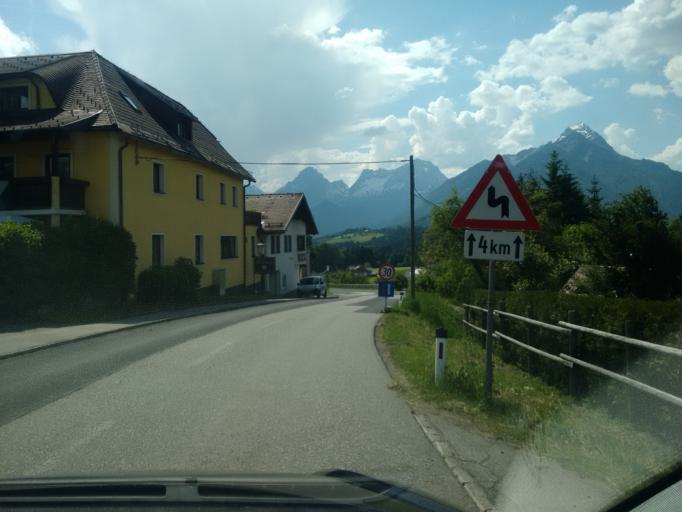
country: AT
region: Upper Austria
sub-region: Politischer Bezirk Kirchdorf an der Krems
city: Rossleithen
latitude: 47.7124
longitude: 14.2225
